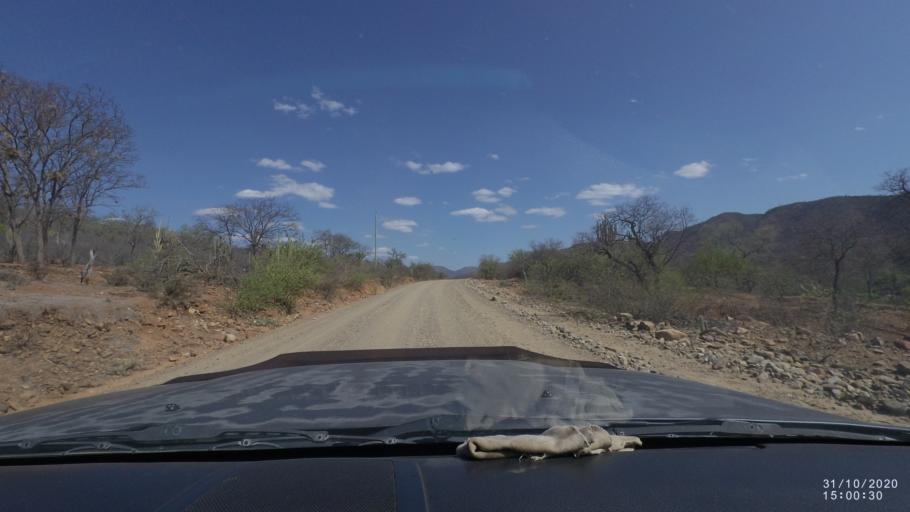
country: BO
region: Cochabamba
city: Aiquile
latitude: -18.2580
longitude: -64.8244
